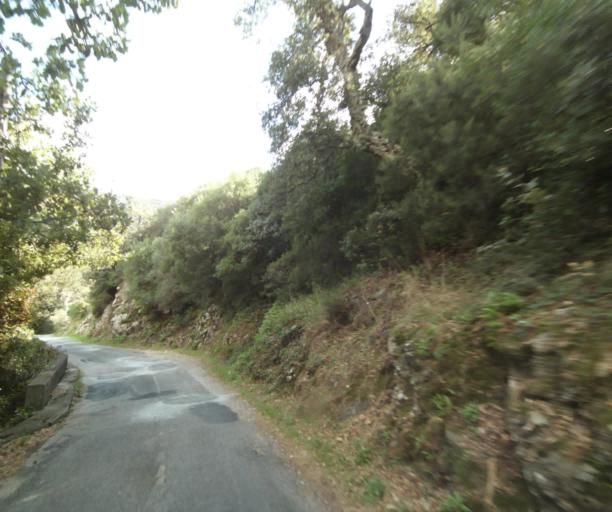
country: FR
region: Languedoc-Roussillon
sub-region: Departement des Pyrenees-Orientales
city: Sorede
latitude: 42.5229
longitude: 2.9880
